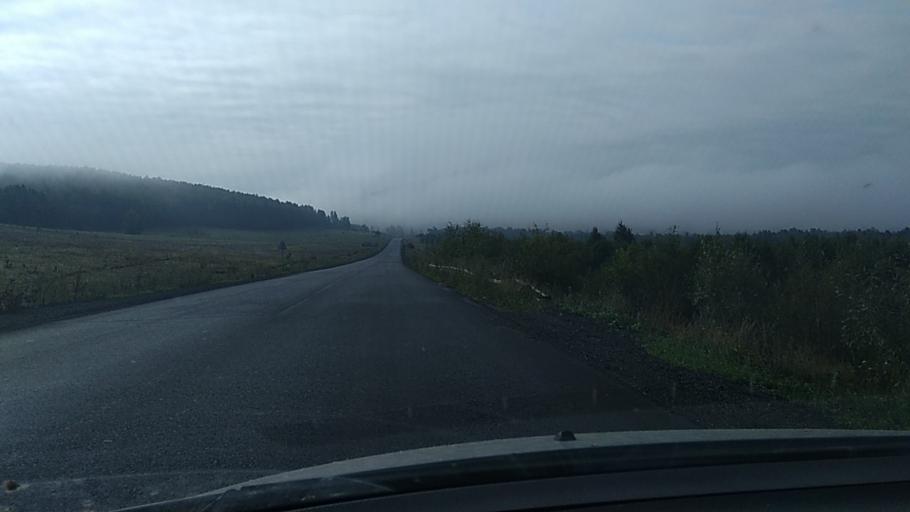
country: RU
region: Chelyabinsk
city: Karabash
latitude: 55.3512
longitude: 60.2443
